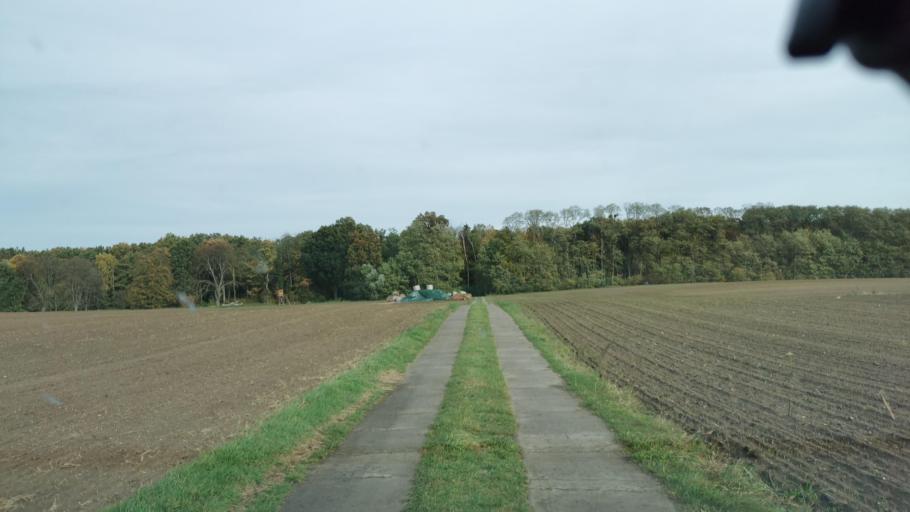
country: DE
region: Brandenburg
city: Eberswalde
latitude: 52.7818
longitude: 13.8564
